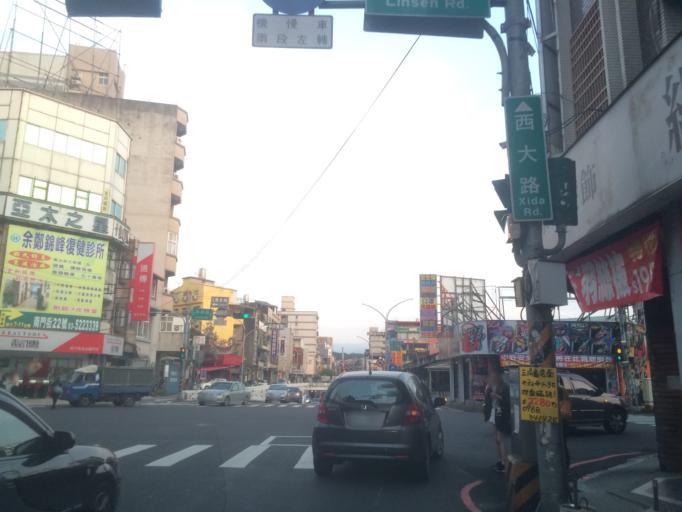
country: TW
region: Taiwan
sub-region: Hsinchu
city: Hsinchu
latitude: 24.8007
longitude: 120.9665
